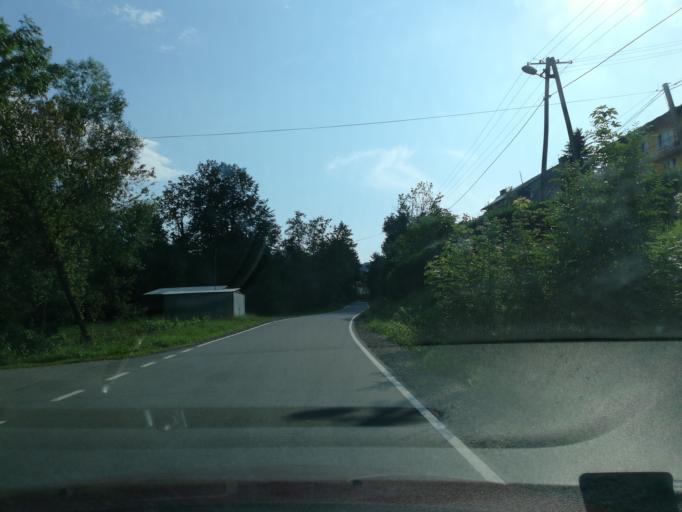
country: PL
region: Lesser Poland Voivodeship
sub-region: Powiat nowosadecki
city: Nawojowa
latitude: 49.5455
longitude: 20.7432
